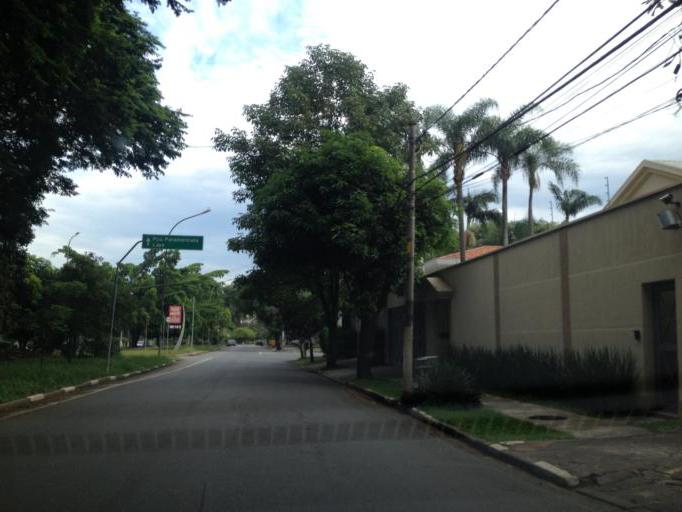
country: BR
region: Sao Paulo
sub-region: Sao Paulo
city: Sao Paulo
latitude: -23.5564
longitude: -46.7075
